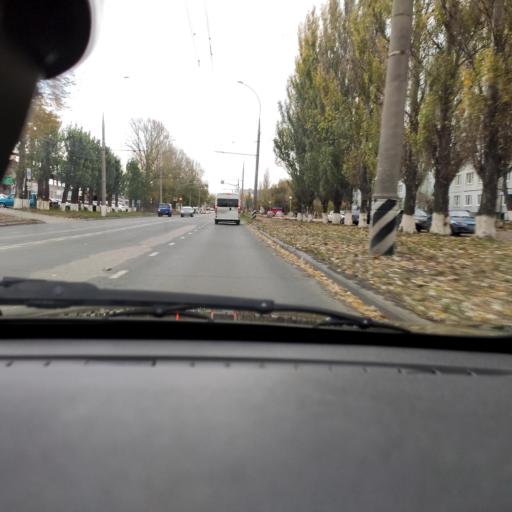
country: RU
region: Samara
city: Tol'yatti
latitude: 53.5367
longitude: 49.2935
